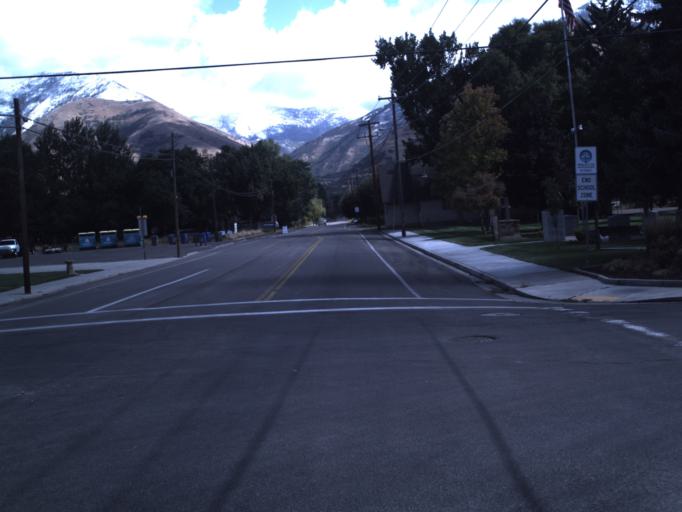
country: US
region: Utah
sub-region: Utah County
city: Mapleton
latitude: 40.1304
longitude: -111.5790
